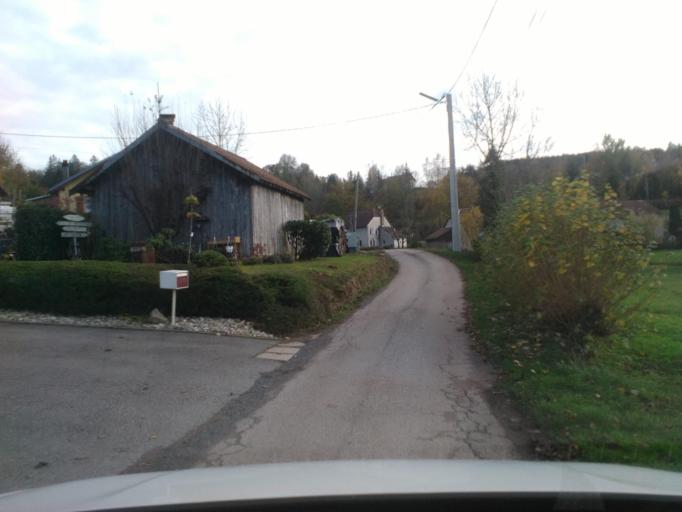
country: FR
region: Lorraine
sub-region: Departement des Vosges
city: Senones
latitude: 48.4103
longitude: 7.0550
